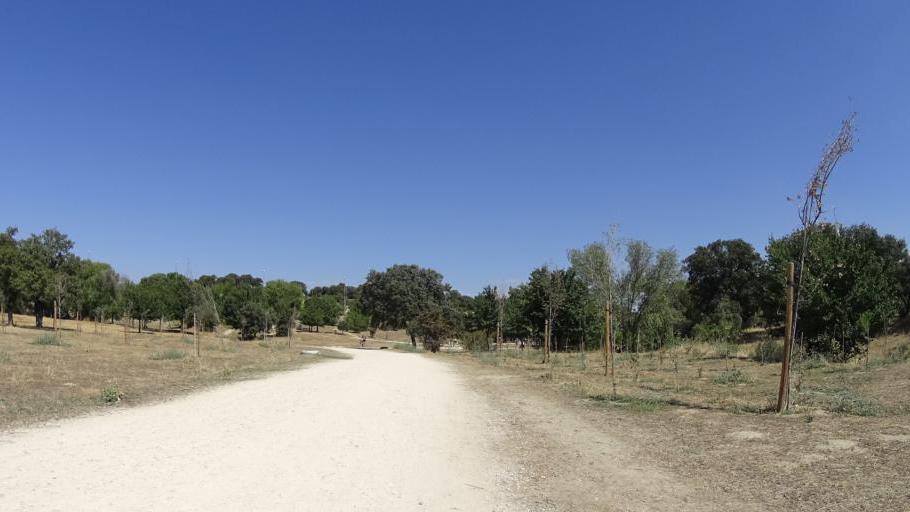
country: ES
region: Madrid
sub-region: Provincia de Madrid
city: Boadilla del Monte
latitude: 40.4079
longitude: -3.8708
